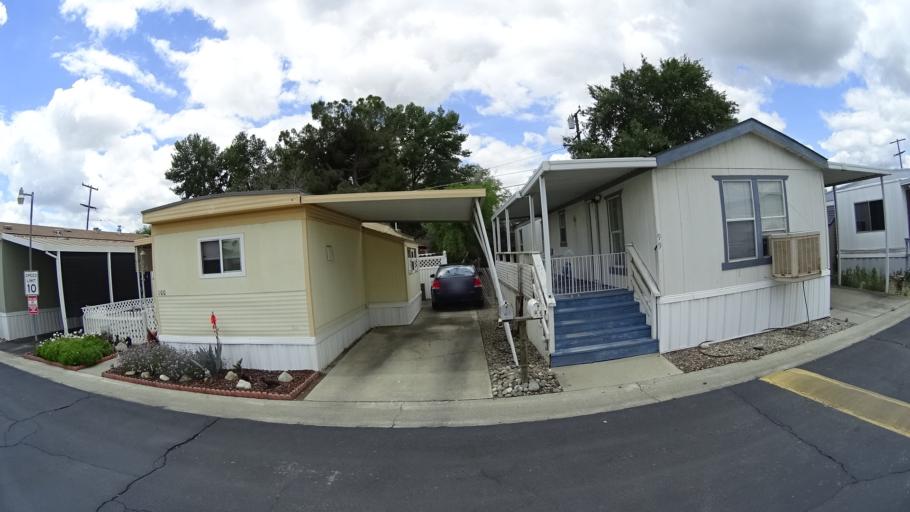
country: US
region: California
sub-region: Kings County
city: Hanford
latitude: 36.3452
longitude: -119.6345
